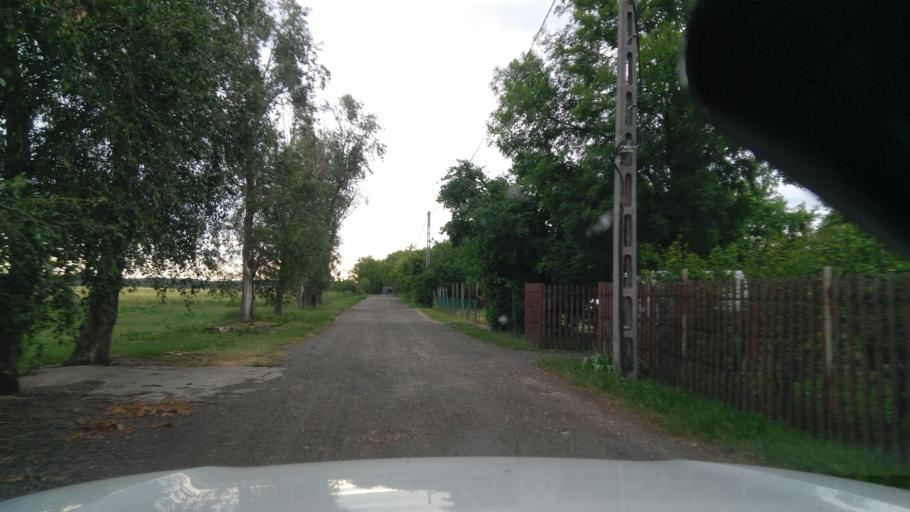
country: HU
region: Bekes
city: Bekescsaba
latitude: 46.6741
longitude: 21.1793
